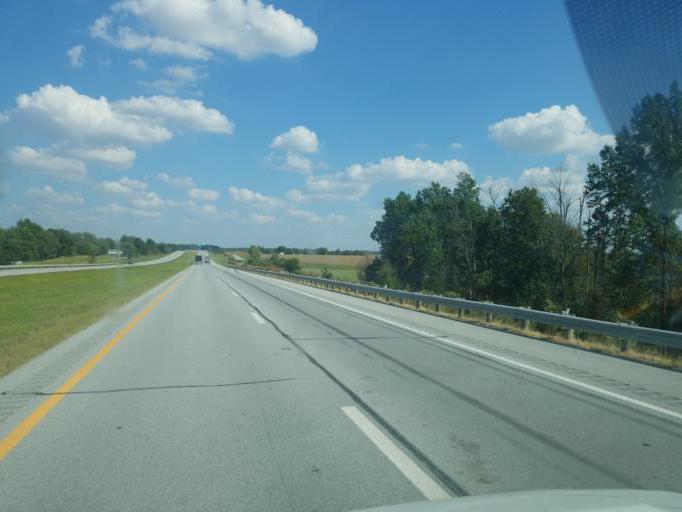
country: US
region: Ohio
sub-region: Putnam County
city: Columbus Grove
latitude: 40.8248
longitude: -83.9866
